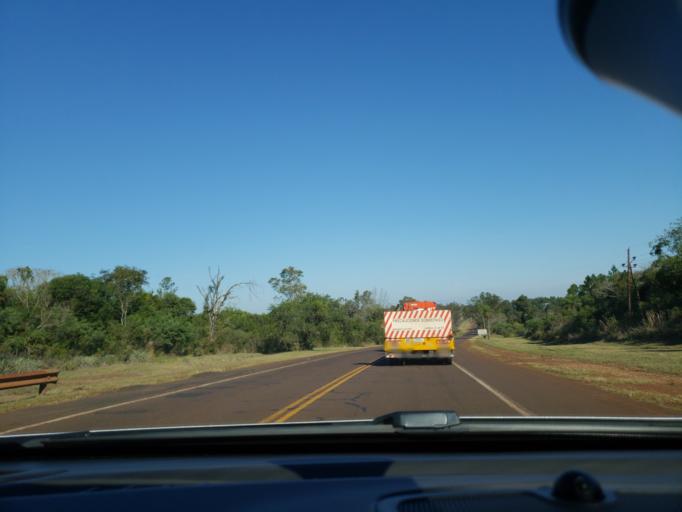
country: AR
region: Misiones
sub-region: Departamento de Apostoles
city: San Jose
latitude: -27.8053
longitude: -55.7676
